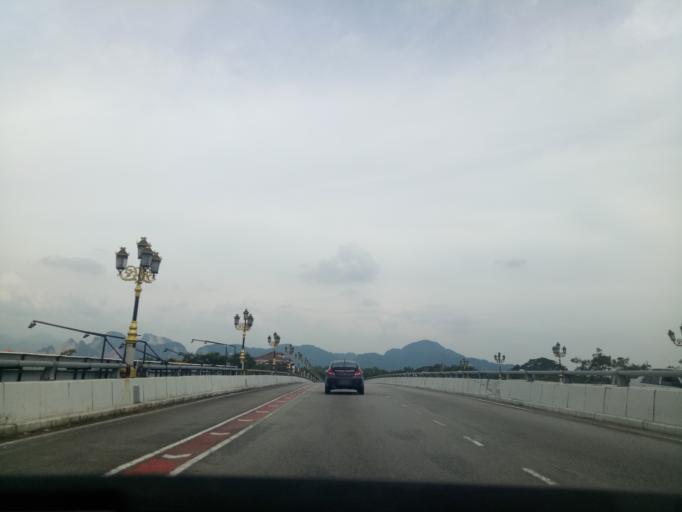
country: MY
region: Perak
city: Ipoh
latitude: 4.6026
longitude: 101.1190
